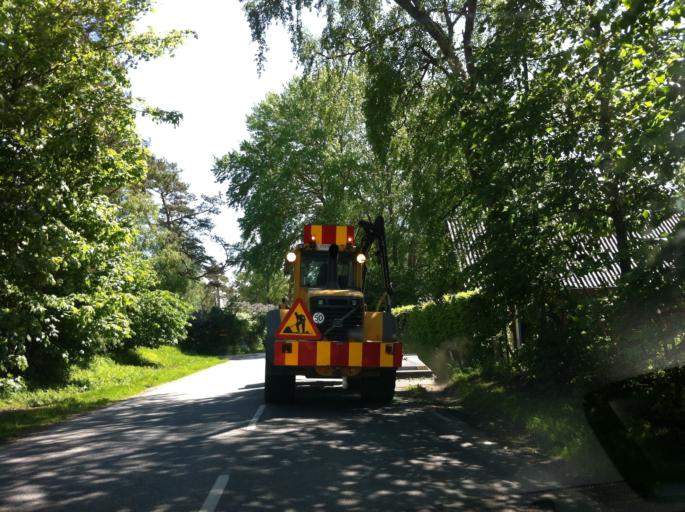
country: SE
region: Skane
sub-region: Kavlinge Kommun
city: Hofterup
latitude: 55.8072
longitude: 12.9820
